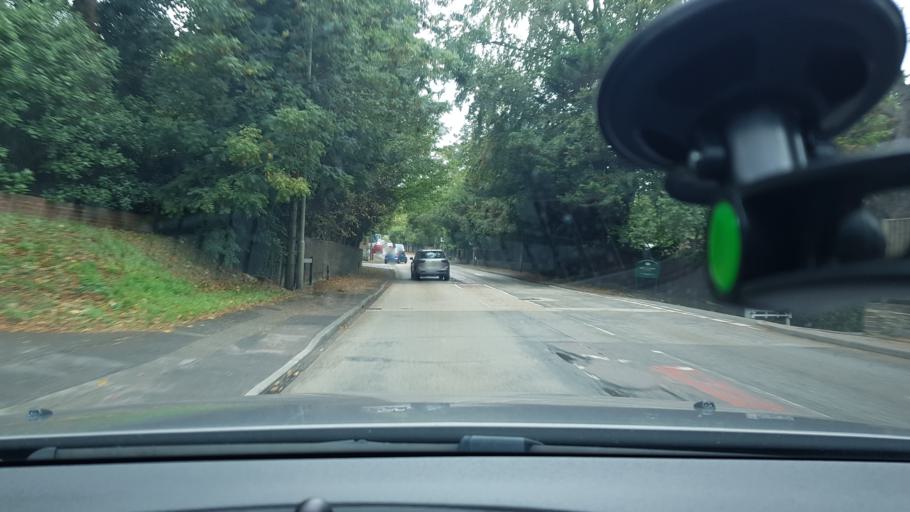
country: GB
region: England
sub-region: Hertfordshire
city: Chorleywood
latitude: 51.6536
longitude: -0.4876
